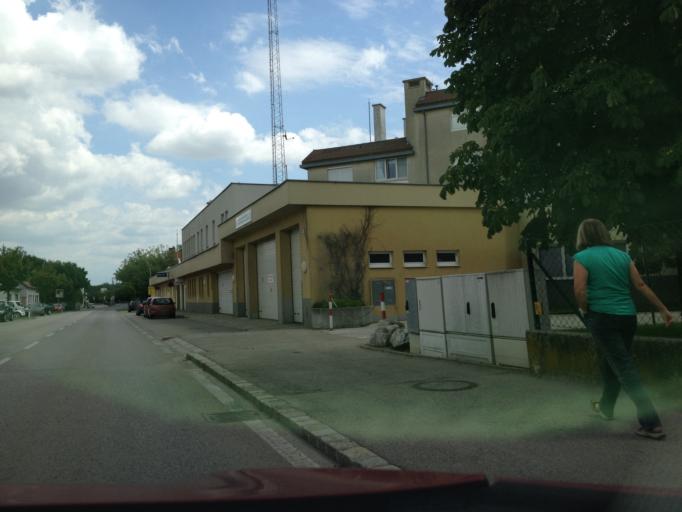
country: AT
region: Lower Austria
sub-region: Politischer Bezirk Baden
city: Gunselsdorf
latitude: 47.9440
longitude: 16.2569
